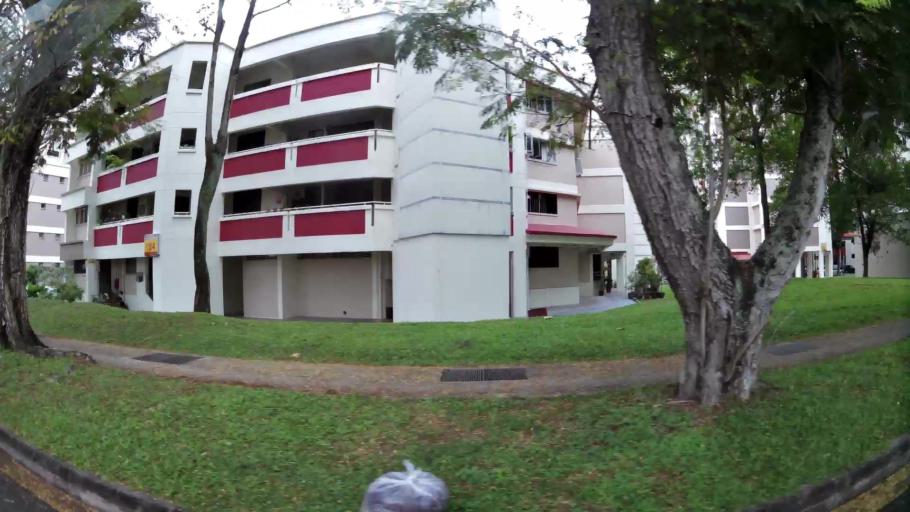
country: SG
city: Singapore
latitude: 1.3661
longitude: 103.8710
